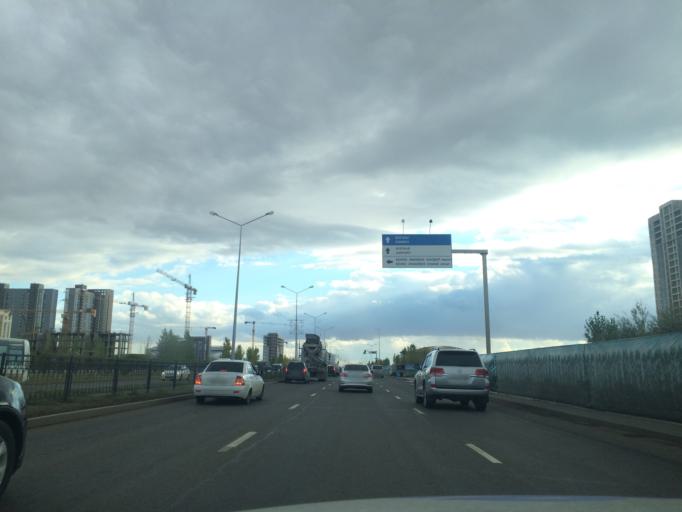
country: KZ
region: Astana Qalasy
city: Astana
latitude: 51.1198
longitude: 71.4021
